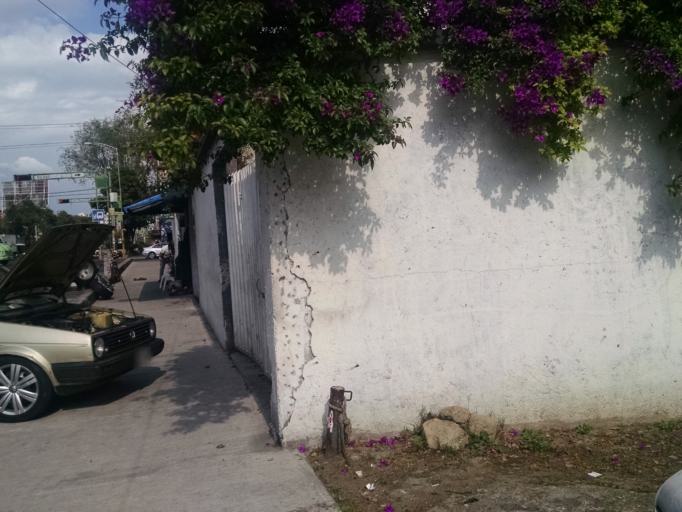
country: MX
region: Mexico City
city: Benito Juarez
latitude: 19.4072
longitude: -99.1428
